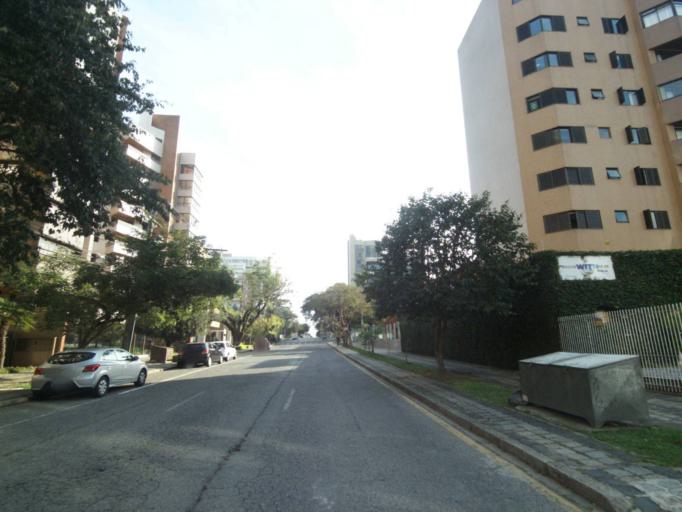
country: BR
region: Parana
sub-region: Curitiba
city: Curitiba
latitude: -25.4323
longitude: -49.2912
